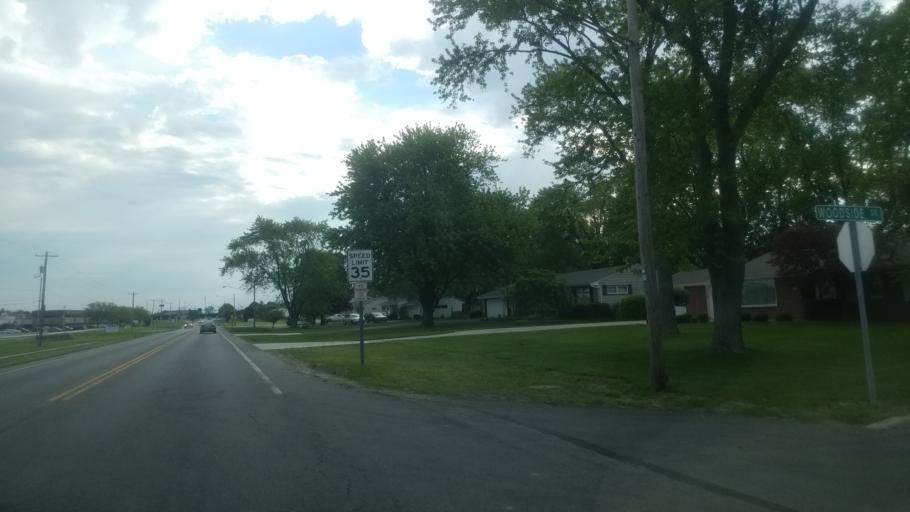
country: US
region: Ohio
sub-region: Hancock County
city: Findlay
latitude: 41.0553
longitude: -83.6217
